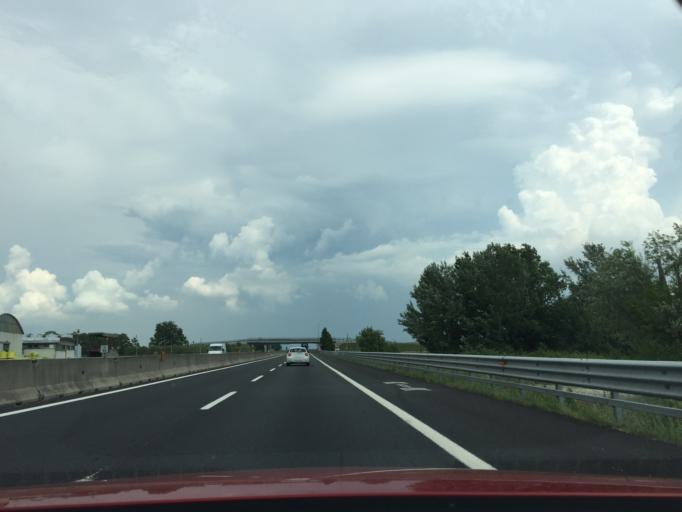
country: IT
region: Tuscany
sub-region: Provincia di Lucca
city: Porcari
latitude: 43.8199
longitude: 10.6200
